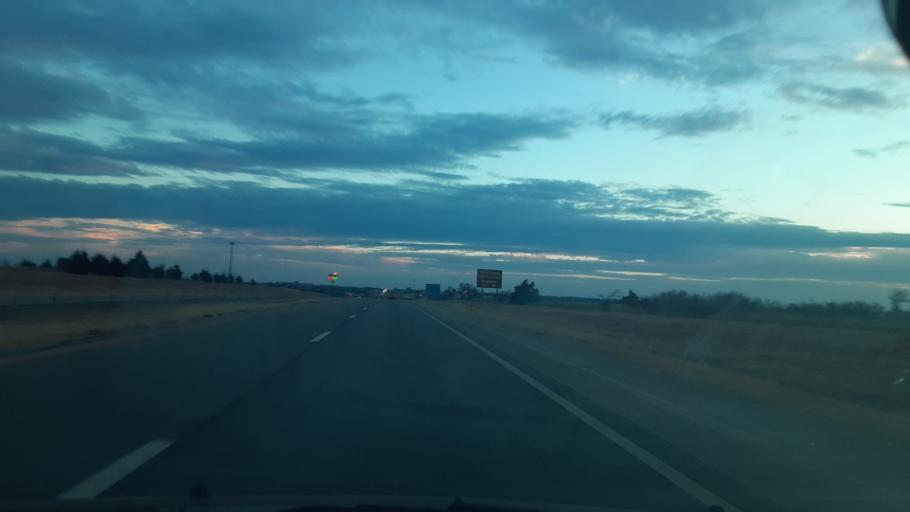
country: US
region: Oklahoma
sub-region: Logan County
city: Guthrie
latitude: 35.8914
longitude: -97.3943
